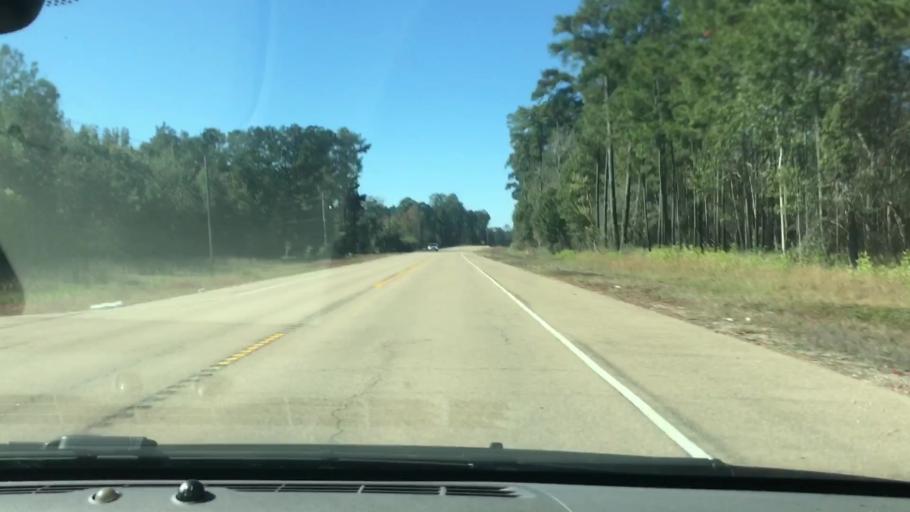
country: US
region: Louisiana
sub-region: Saint Tammany Parish
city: Abita Springs
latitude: 30.5057
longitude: -89.9720
